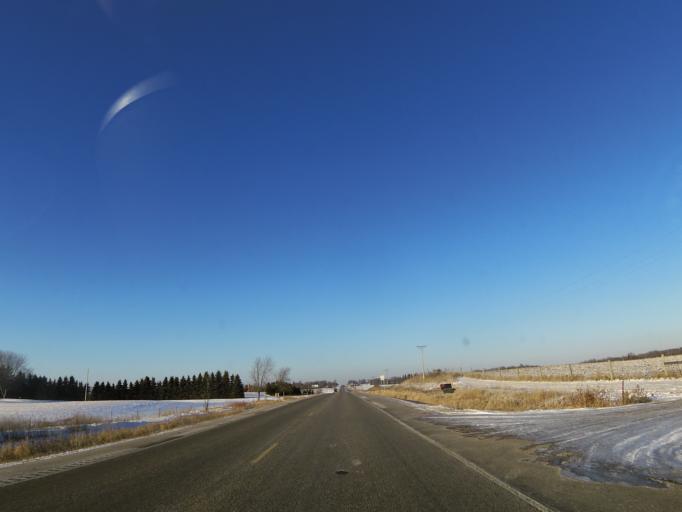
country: US
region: Minnesota
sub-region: Rice County
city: Lonsdale
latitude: 44.5044
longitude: -93.4428
